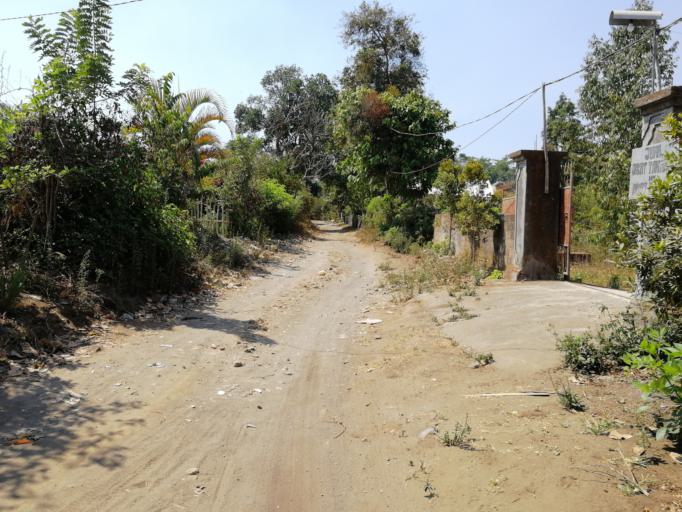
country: ID
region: West Nusa Tenggara
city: Lelongken
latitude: -8.3219
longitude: 116.4902
